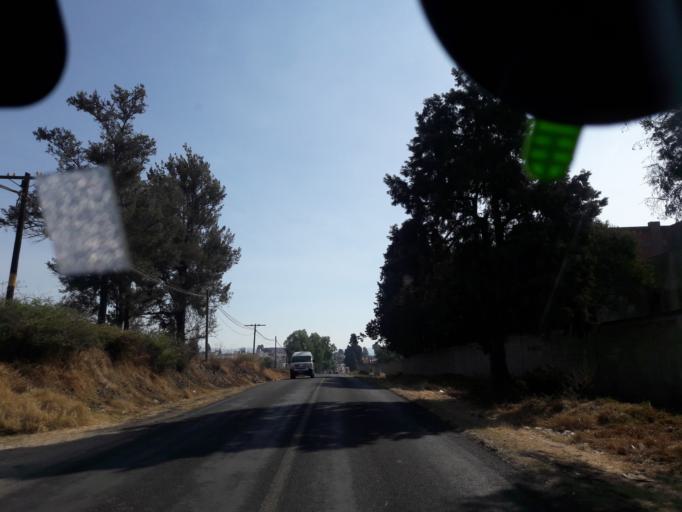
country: MX
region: Tlaxcala
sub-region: Ixtacuixtla de Mariano Matamoros
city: Villa Mariano Matamoros
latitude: 19.3112
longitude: -98.3940
